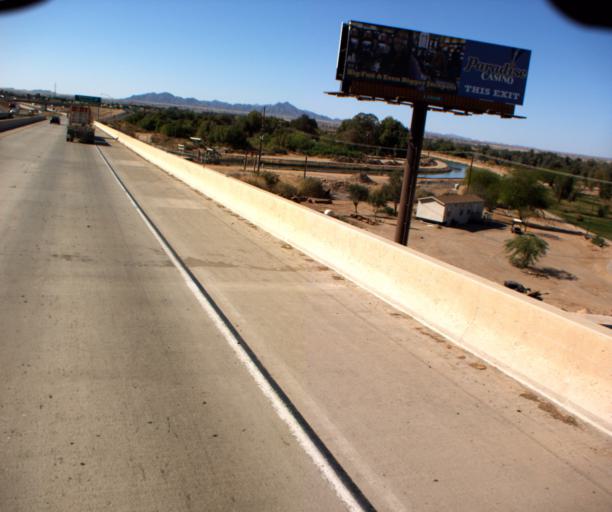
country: US
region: Arizona
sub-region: Yuma County
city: Yuma
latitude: 32.7293
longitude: -114.6189
